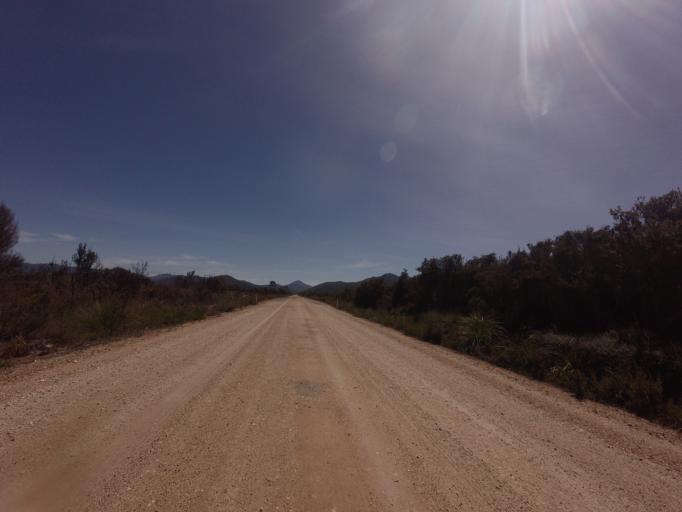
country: AU
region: Tasmania
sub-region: Huon Valley
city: Geeveston
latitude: -42.9722
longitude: 146.3648
